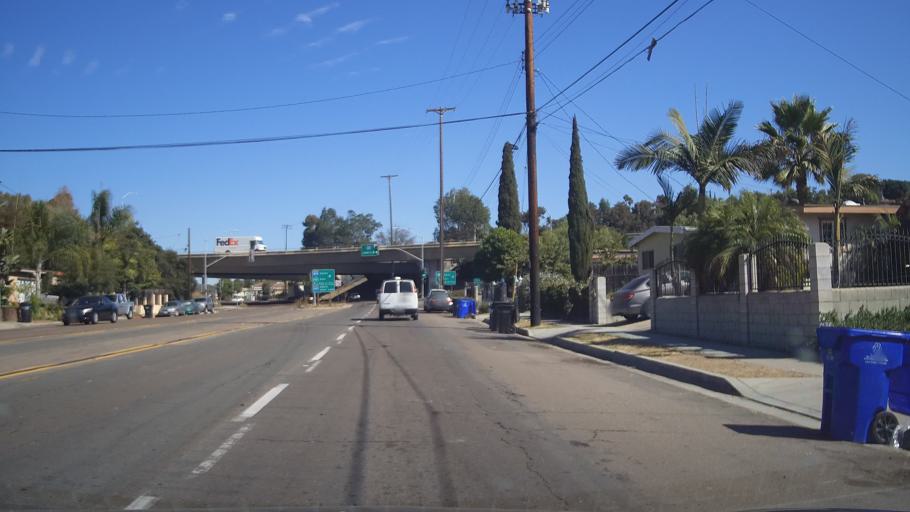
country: US
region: California
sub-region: San Diego County
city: National City
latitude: 32.7247
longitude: -117.1047
